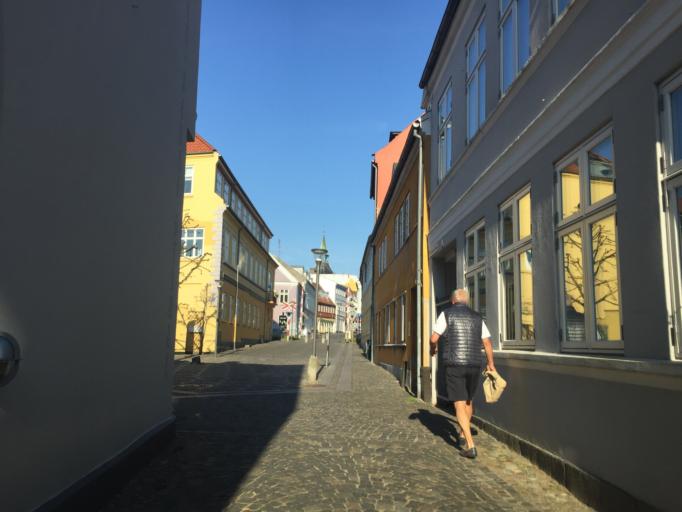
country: DK
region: South Denmark
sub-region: Svendborg Kommune
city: Svendborg
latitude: 55.0585
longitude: 10.6131
